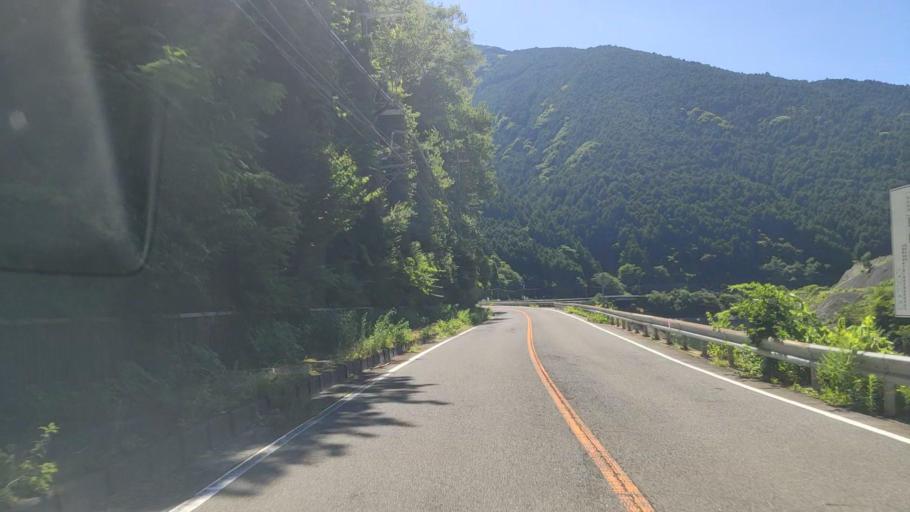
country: JP
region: Nara
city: Yoshino-cho
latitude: 34.3116
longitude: 135.9829
